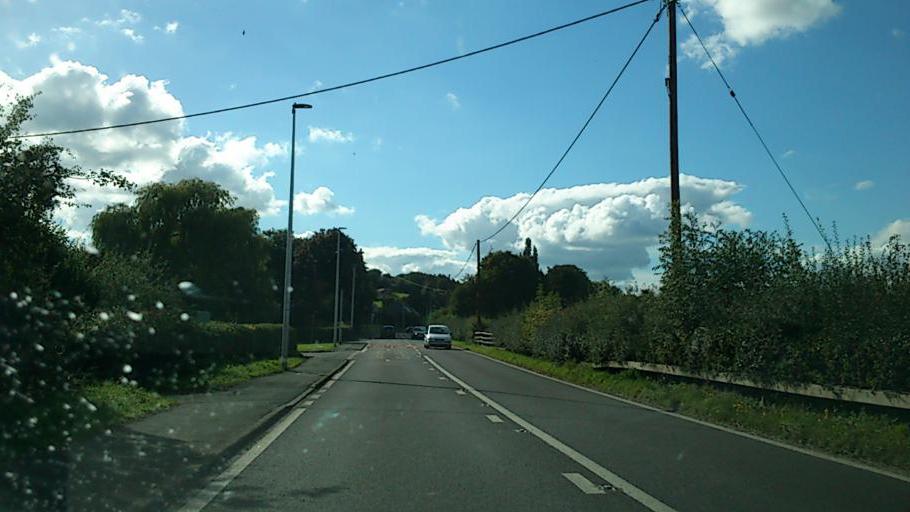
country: GB
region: Wales
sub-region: Sir Powys
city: Welshpool
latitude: 52.6896
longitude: -3.0746
